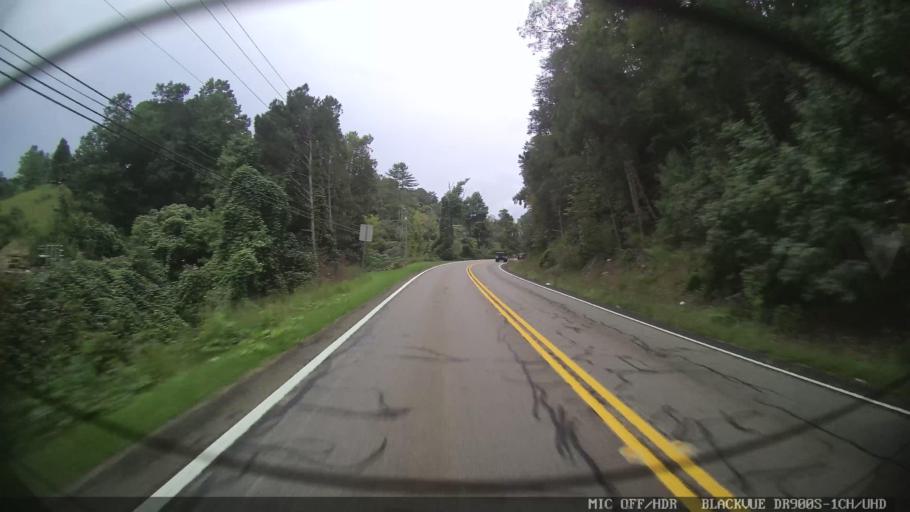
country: US
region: Georgia
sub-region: Gilmer County
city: Ellijay
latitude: 34.7049
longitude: -84.4884
